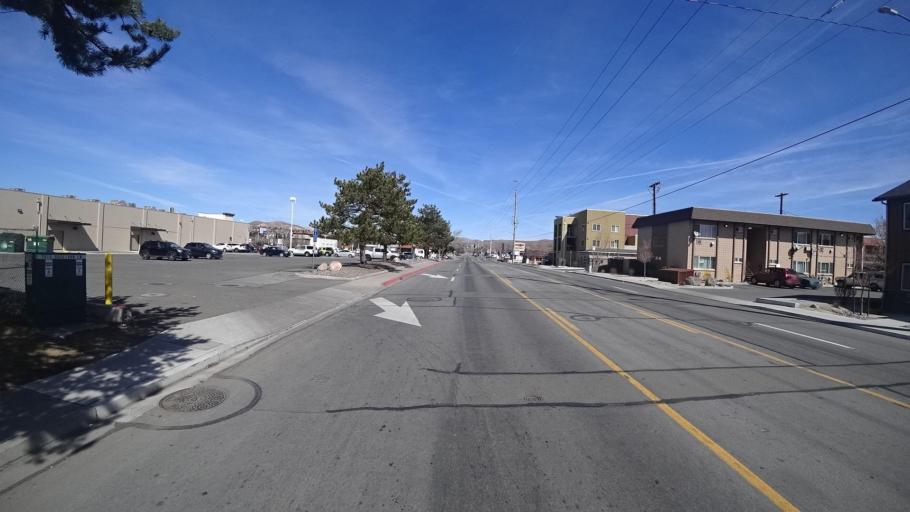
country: US
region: Nevada
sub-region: Washoe County
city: Sparks
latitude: 39.5438
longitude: -119.7716
